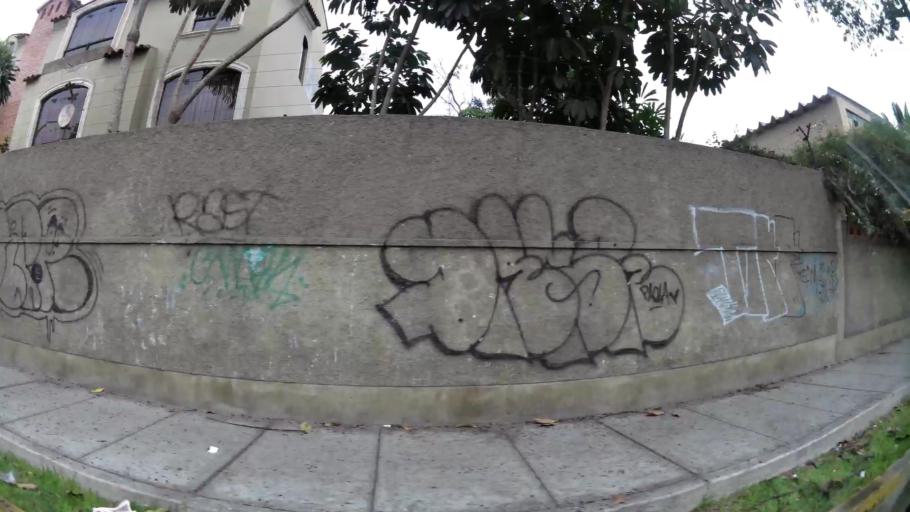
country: PE
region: Lima
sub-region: Lima
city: Surco
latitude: -12.1708
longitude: -77.0202
